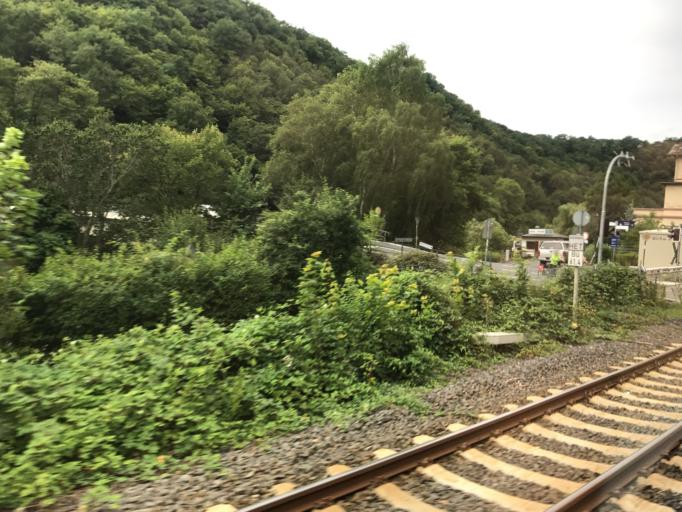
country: DE
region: Rheinland-Pfalz
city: Balduinstein
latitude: 50.3462
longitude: 7.9690
